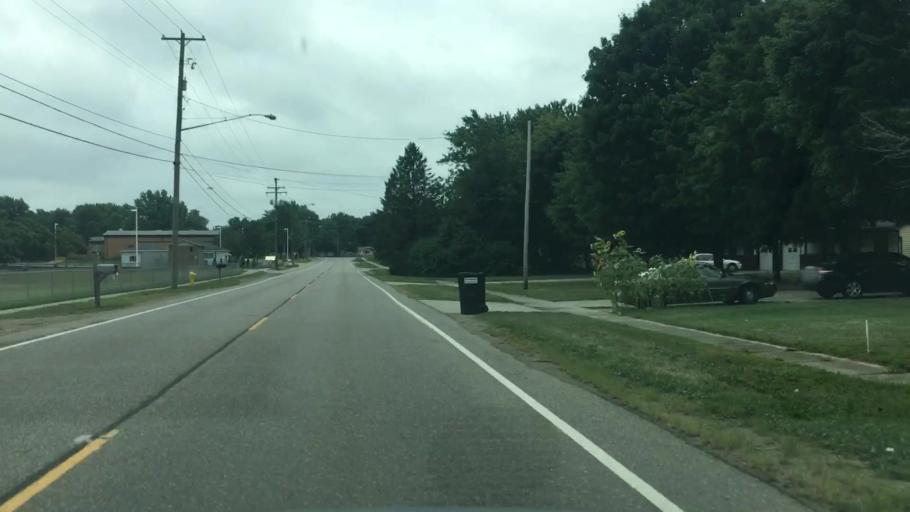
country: US
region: Michigan
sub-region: Ottawa County
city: Jenison
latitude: 42.8918
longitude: -85.8119
